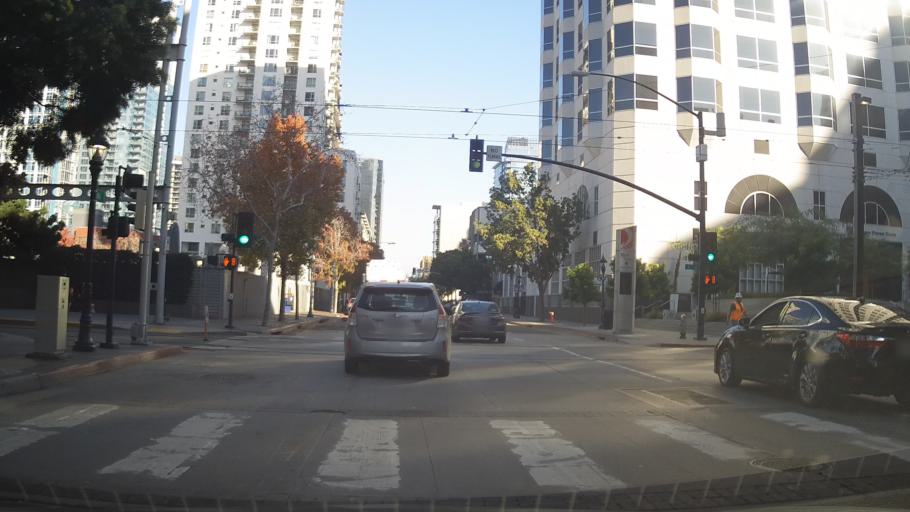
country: US
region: California
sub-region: San Diego County
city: San Diego
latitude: 32.7165
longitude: -117.1684
